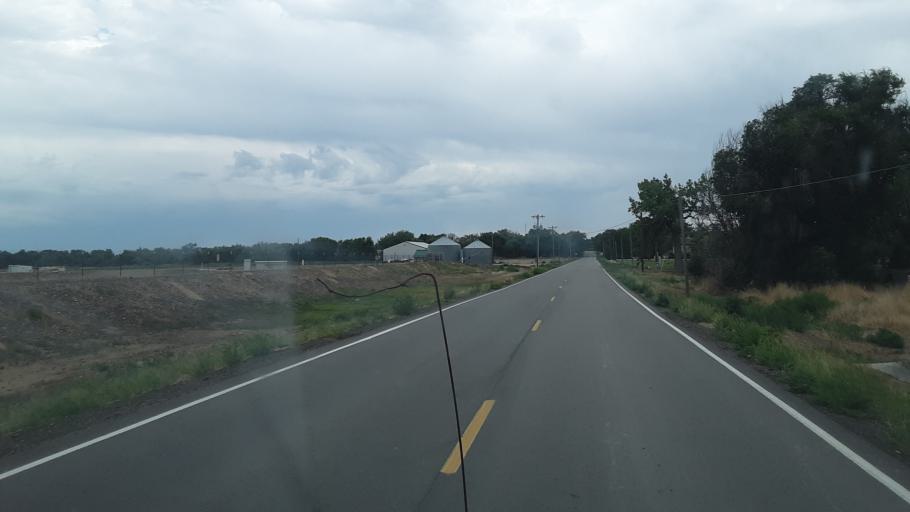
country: US
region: Colorado
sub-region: Otero County
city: Fowler
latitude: 38.1390
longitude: -104.0222
